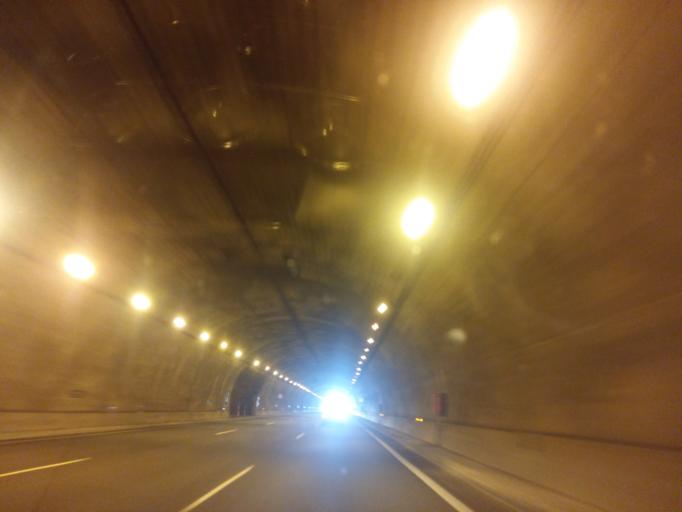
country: ES
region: Cantabria
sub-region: Provincia de Cantabria
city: Cartes
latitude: 43.3045
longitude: -4.0788
